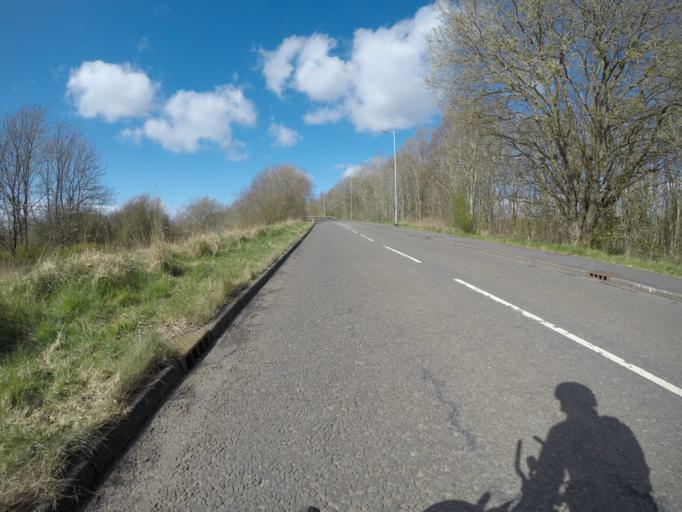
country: GB
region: Scotland
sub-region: North Ayrshire
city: Irvine
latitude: 55.6146
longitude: -4.6428
